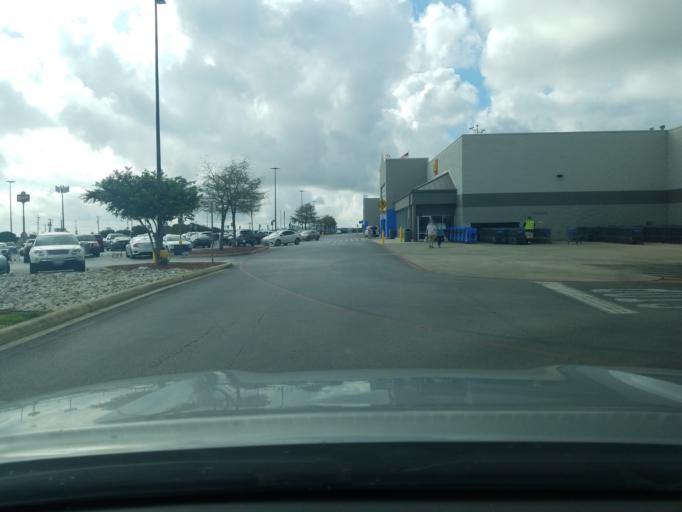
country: US
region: Texas
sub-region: Bexar County
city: Live Oak
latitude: 29.5930
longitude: -98.3559
